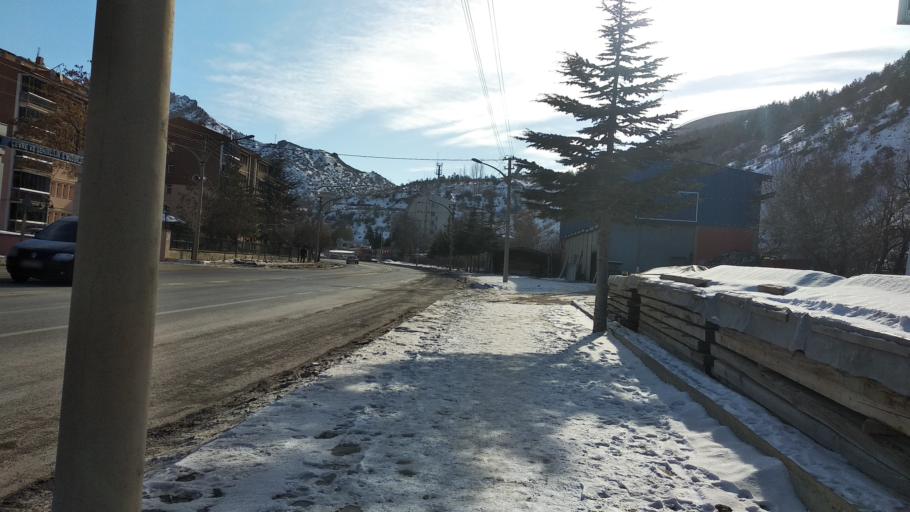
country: TR
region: Gumushane
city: Gumushkhane
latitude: 40.4484
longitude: 39.4968
